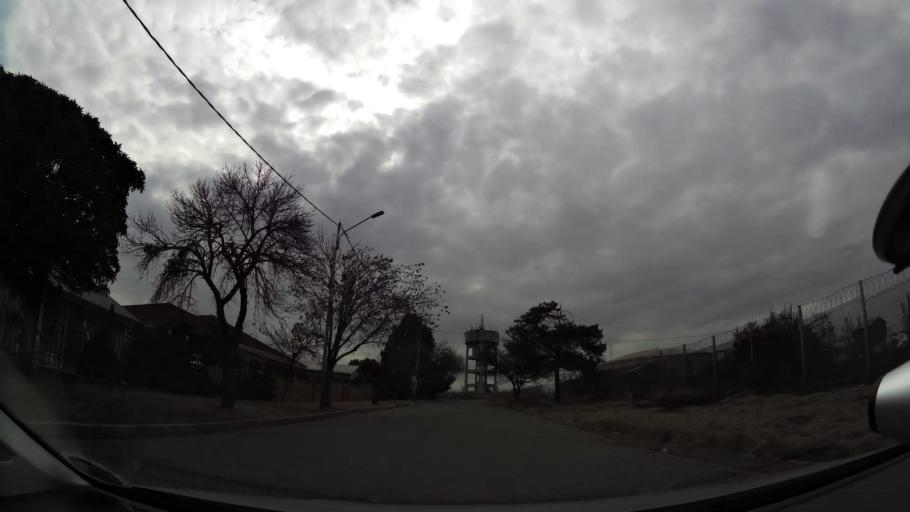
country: ZA
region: Orange Free State
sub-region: Fezile Dabi District Municipality
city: Kroonstad
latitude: -27.6514
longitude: 27.2332
